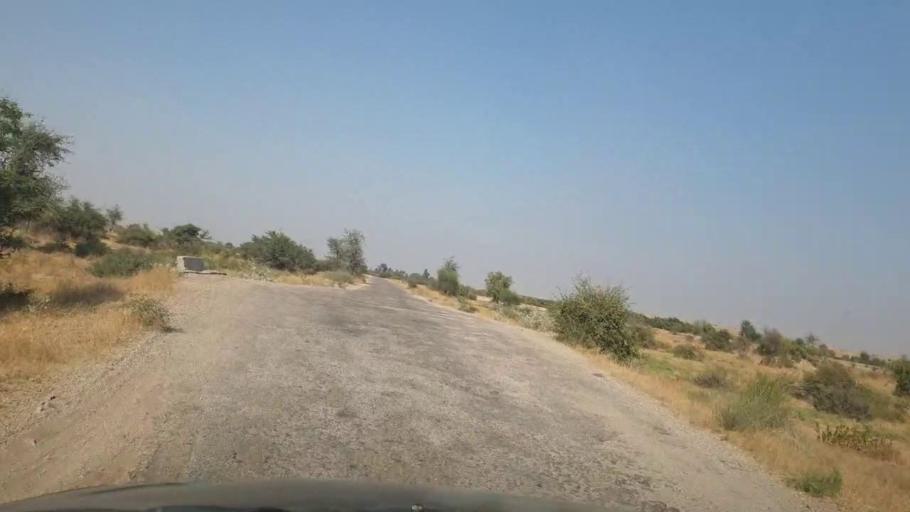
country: PK
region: Sindh
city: Jamshoro
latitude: 25.4840
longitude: 67.8239
